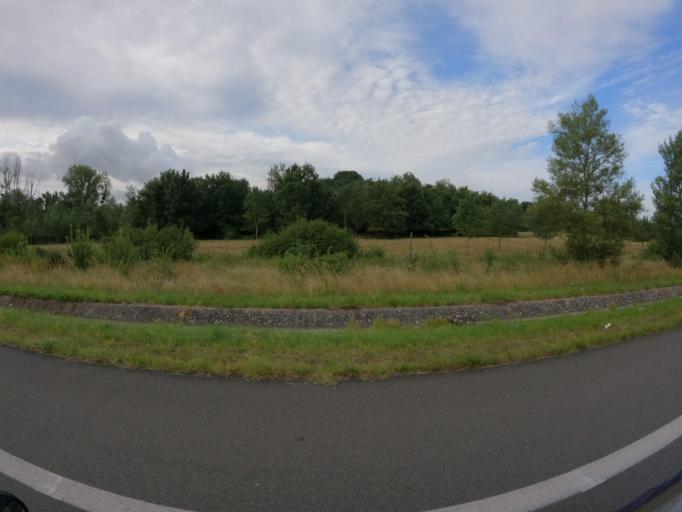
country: FR
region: Centre
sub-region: Departement d'Indre-et-Loire
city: Bourgueil
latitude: 47.2572
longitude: 0.1584
